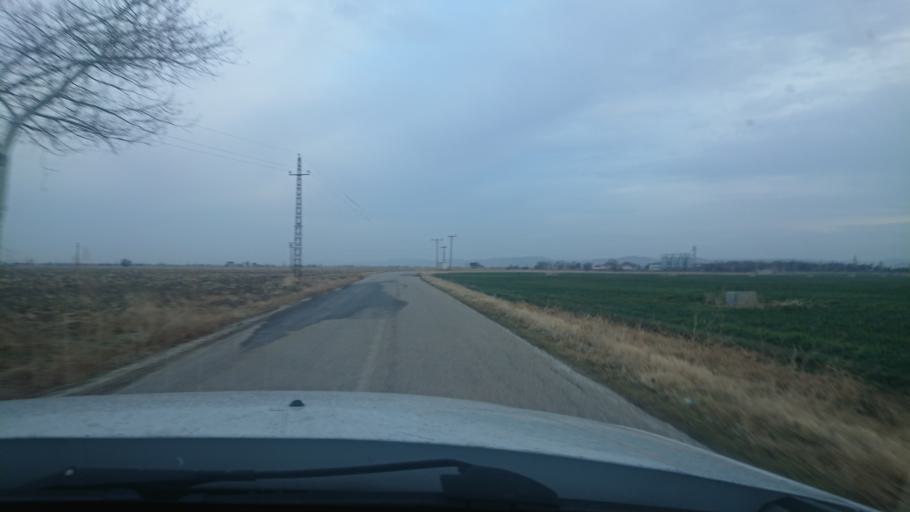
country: TR
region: Aksaray
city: Yesilova
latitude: 38.4486
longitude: 33.8349
